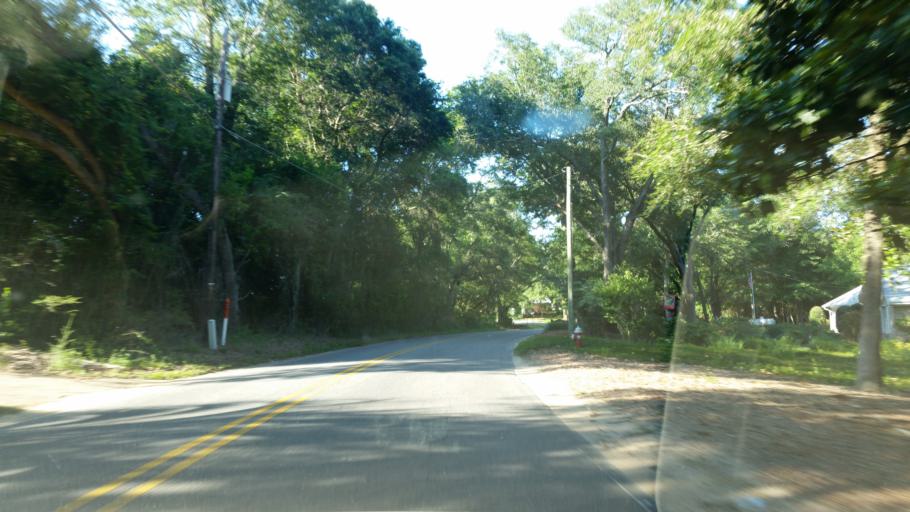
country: US
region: Florida
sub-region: Escambia County
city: Bellview
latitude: 30.5053
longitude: -87.3826
